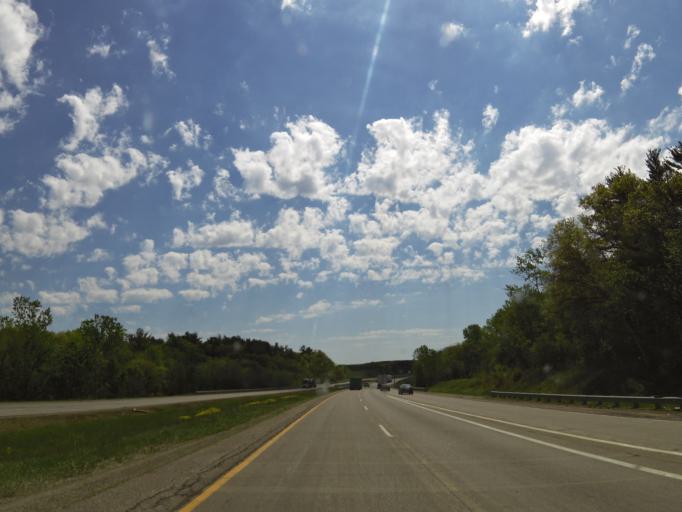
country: US
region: Wisconsin
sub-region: Eau Claire County
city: Altoona
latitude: 44.7666
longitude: -91.4128
